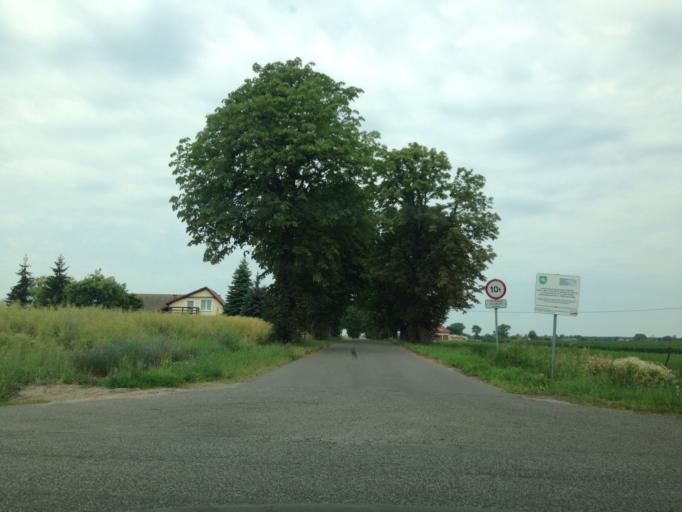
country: PL
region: Kujawsko-Pomorskie
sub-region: Powiat brodnicki
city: Bobrowo
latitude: 53.2147
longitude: 19.2390
